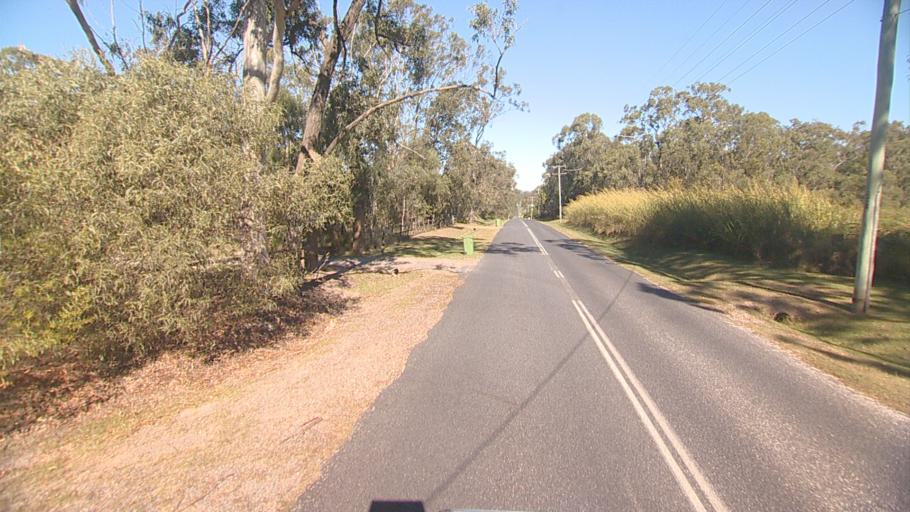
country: AU
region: Queensland
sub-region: Logan
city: Park Ridge South
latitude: -27.7121
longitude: 153.0585
